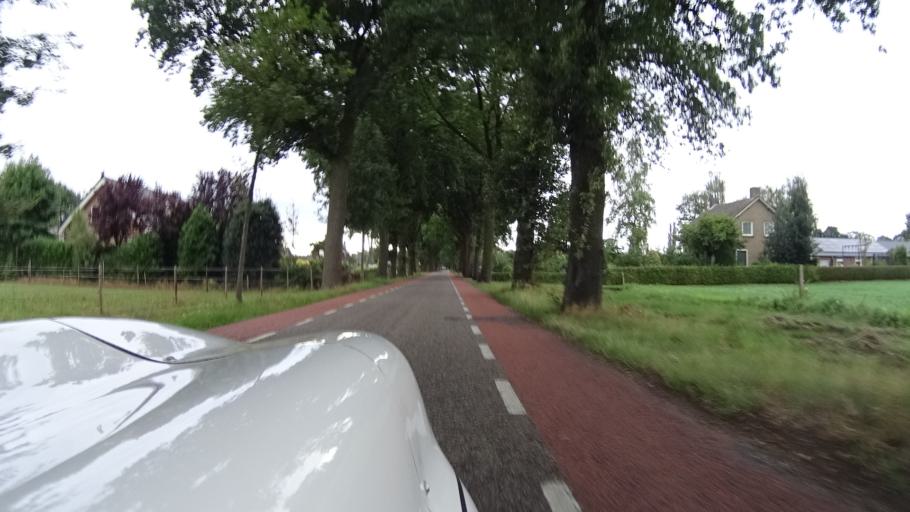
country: NL
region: North Brabant
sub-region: Gemeente Bernheze
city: Loosbroek
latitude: 51.6736
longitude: 5.5293
